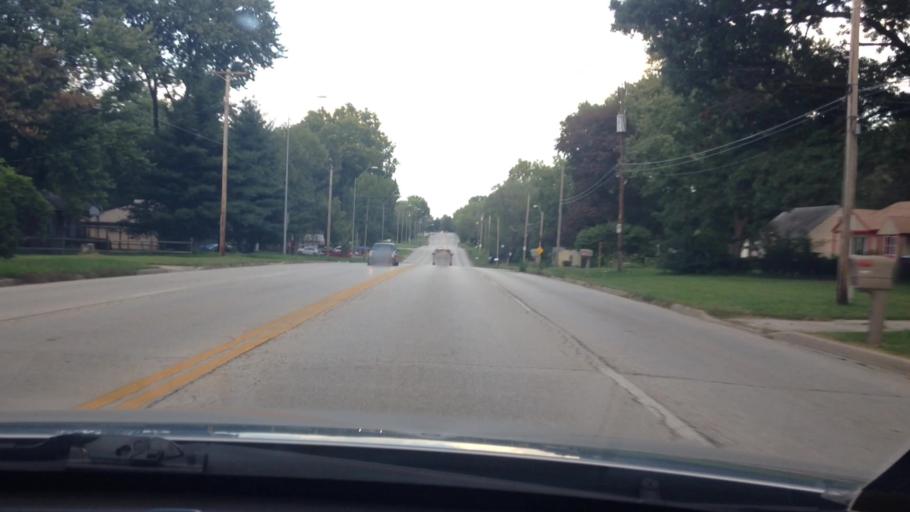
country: US
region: Missouri
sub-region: Jackson County
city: Raytown
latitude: 38.9763
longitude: -94.4911
